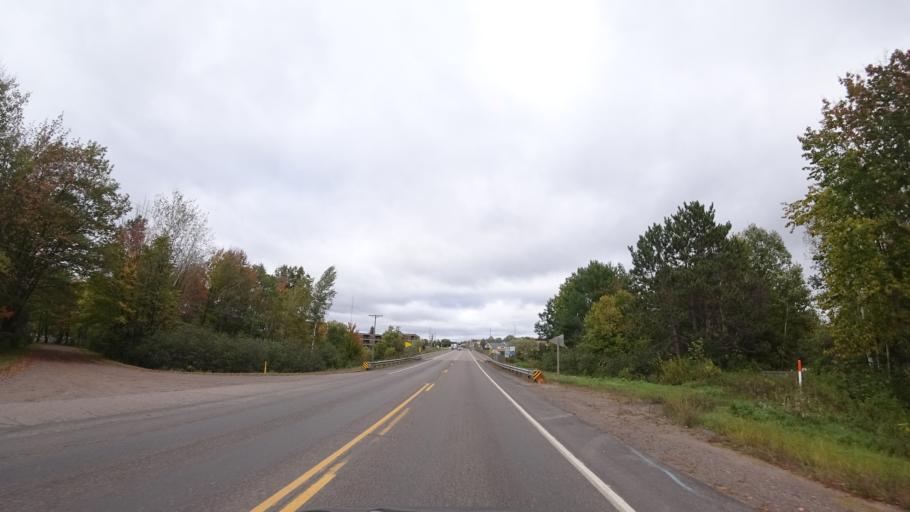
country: US
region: Wisconsin
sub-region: Rusk County
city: Ladysmith
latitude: 45.4522
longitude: -91.1096
